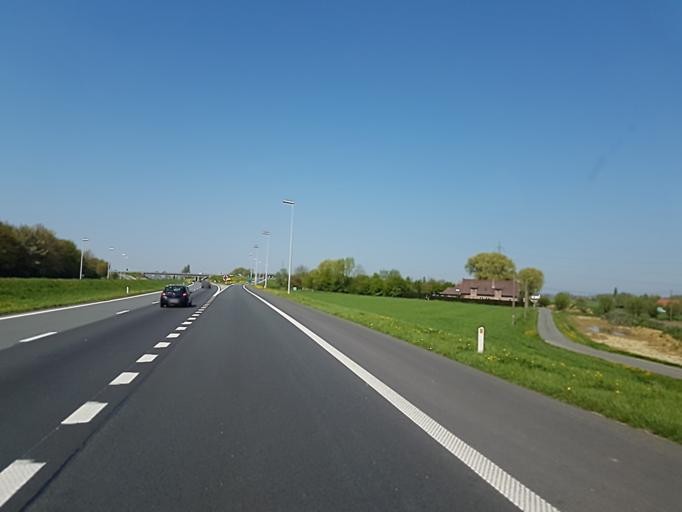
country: BE
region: Flanders
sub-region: Provincie West-Vlaanderen
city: Zonnebeke
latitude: 50.8612
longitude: 2.9626
